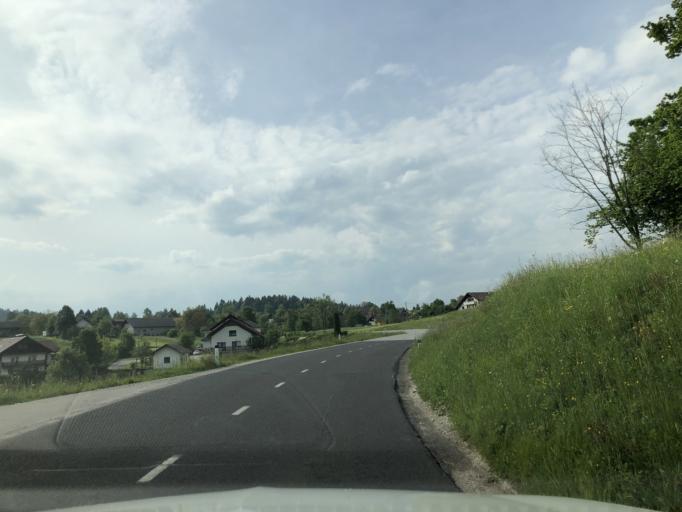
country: SI
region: Velike Lasce
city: Velike Lasce
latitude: 45.8119
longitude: 14.6252
